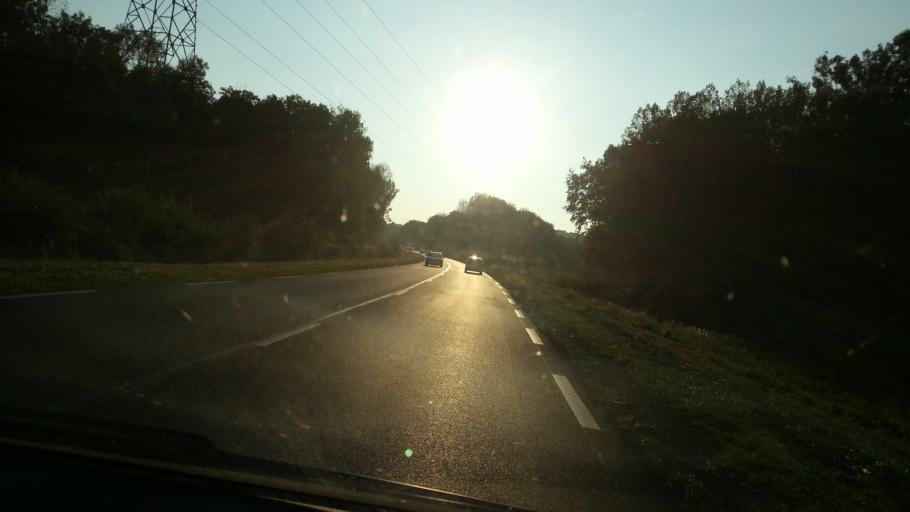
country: FR
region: Picardie
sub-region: Departement de l'Oise
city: Brenouille
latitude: 49.3163
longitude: 2.5620
